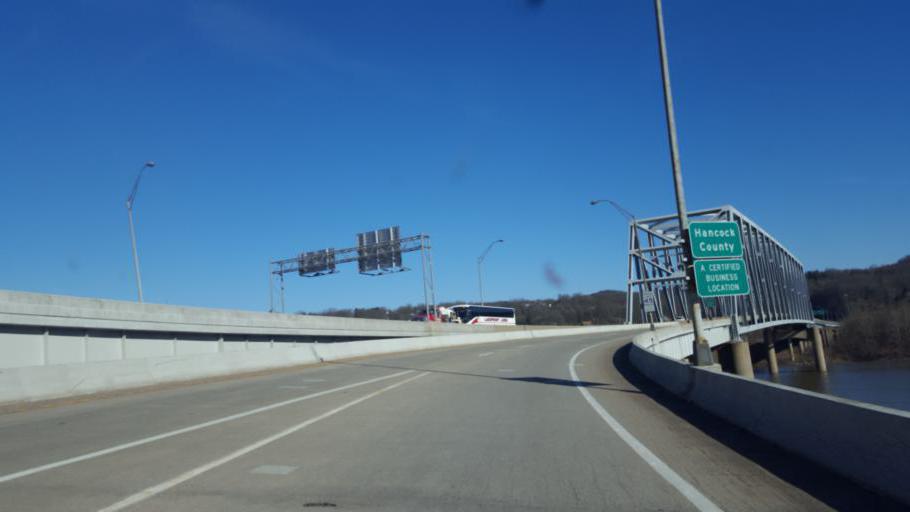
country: US
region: West Virginia
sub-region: Hancock County
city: Chester
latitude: 40.6211
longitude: -80.5638
